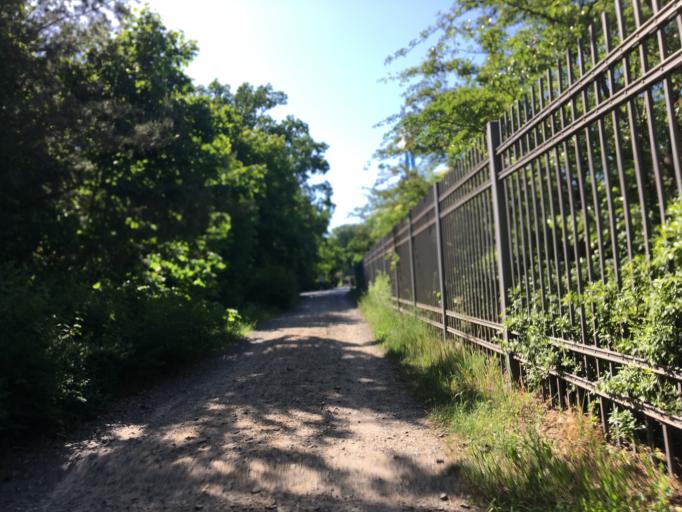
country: DE
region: Berlin
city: Karlshorst
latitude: 52.4682
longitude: 13.5366
